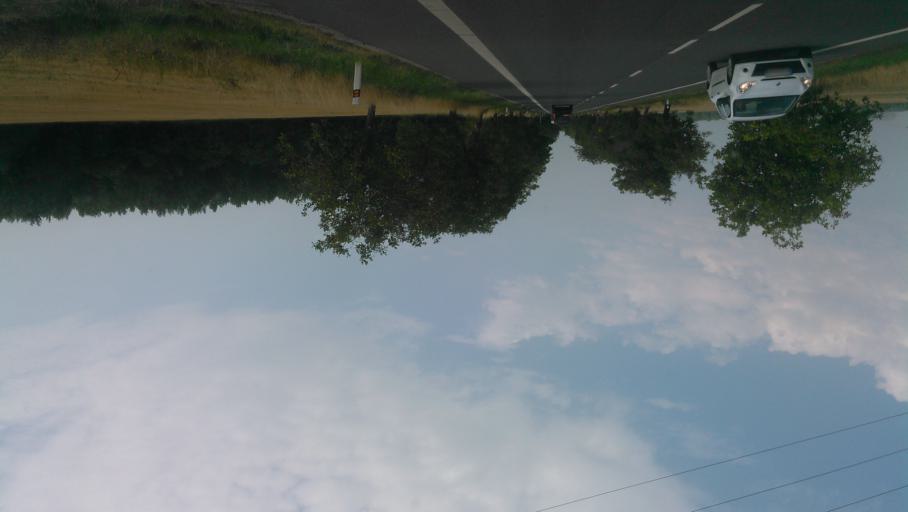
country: SK
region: Trnavsky
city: Dunajska Streda
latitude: 47.9651
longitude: 17.6892
